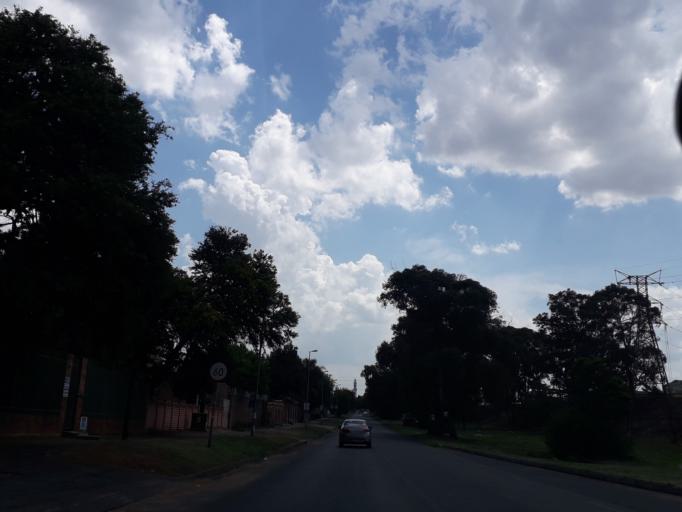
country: ZA
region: Gauteng
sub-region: City of Johannesburg Metropolitan Municipality
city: Johannesburg
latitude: -26.2391
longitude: 28.0167
